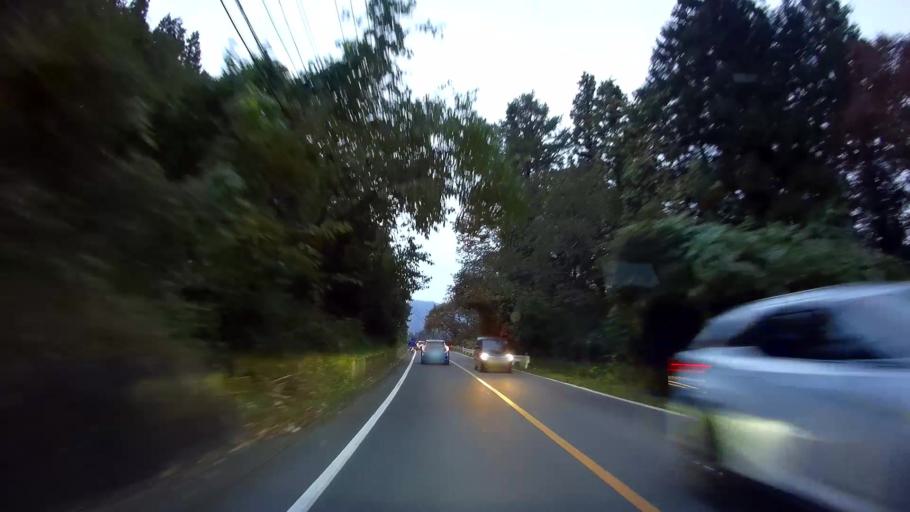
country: JP
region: Gunma
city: Nakanojomachi
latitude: 36.5409
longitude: 138.7919
